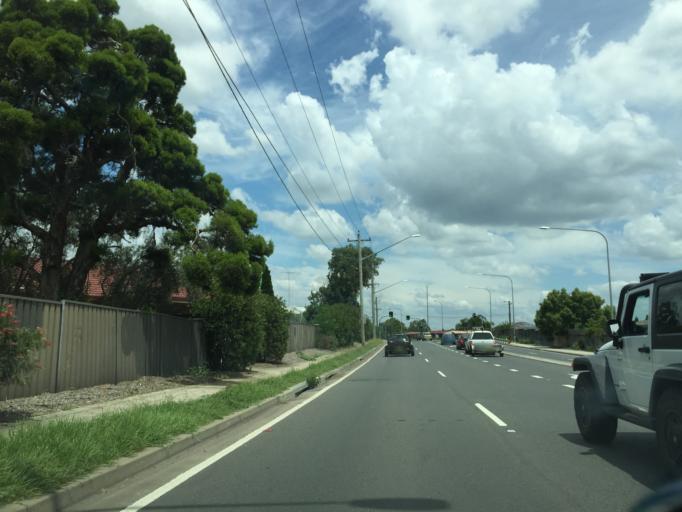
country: AU
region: New South Wales
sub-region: Blacktown
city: Hassall Grove
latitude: -33.7366
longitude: 150.8448
